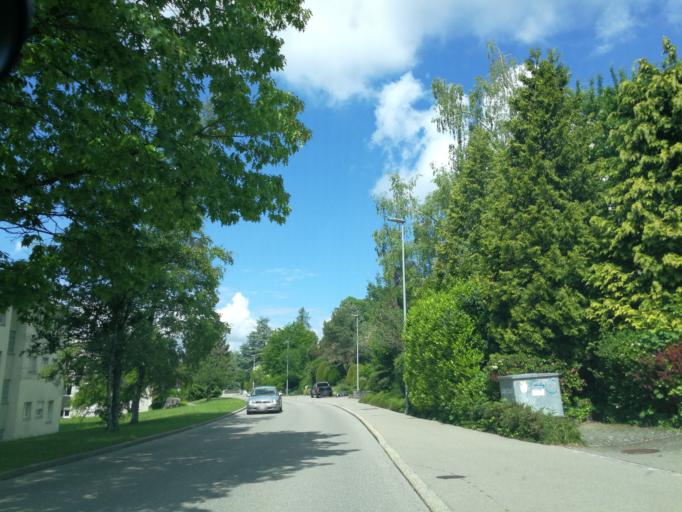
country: CH
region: Zurich
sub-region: Bezirk Meilen
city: Zumikon
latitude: 47.3277
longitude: 8.6339
